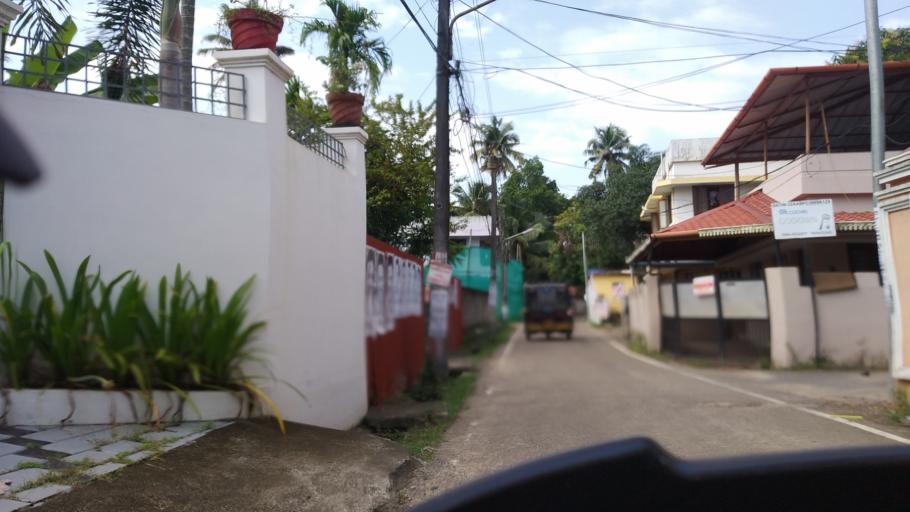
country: IN
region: Kerala
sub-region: Ernakulam
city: Cochin
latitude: 9.9846
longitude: 76.3002
